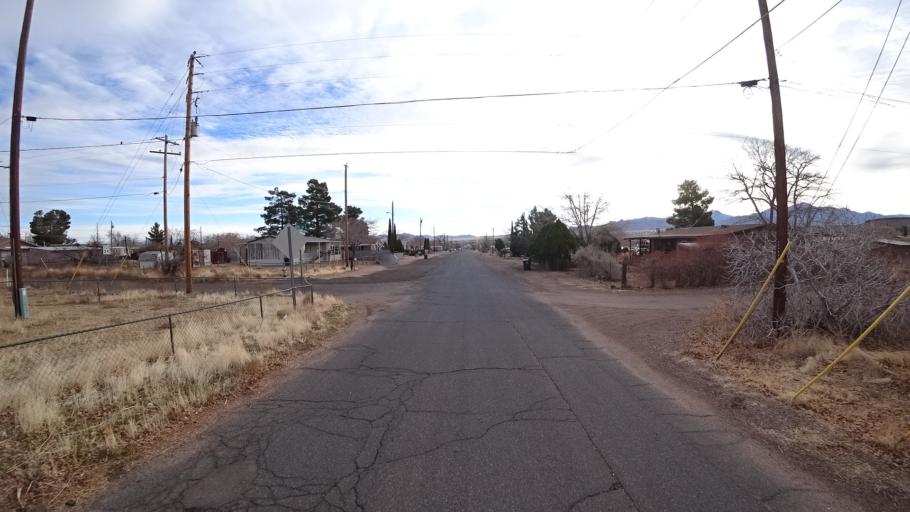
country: US
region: Arizona
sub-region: Mohave County
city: Kingman
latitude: 35.2149
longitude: -114.0535
